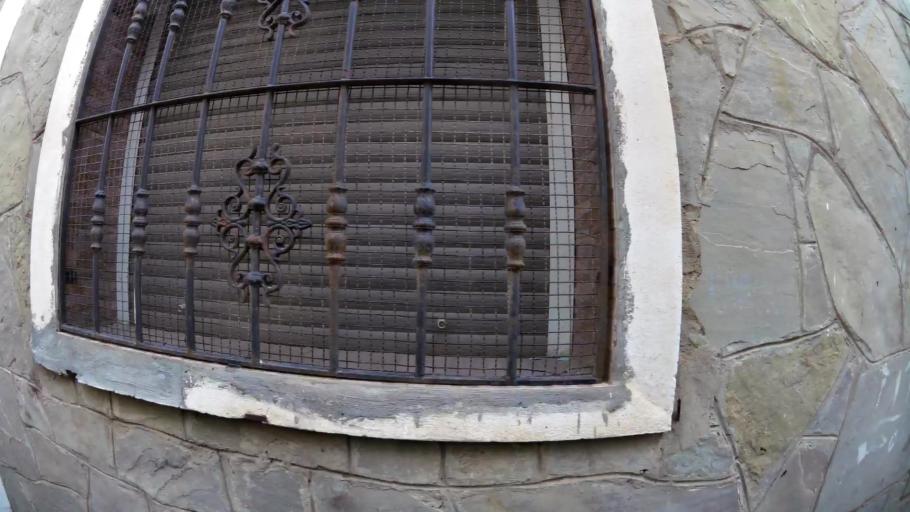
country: MA
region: Tanger-Tetouan
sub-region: Tetouan
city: Martil
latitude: 35.6142
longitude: -5.2794
